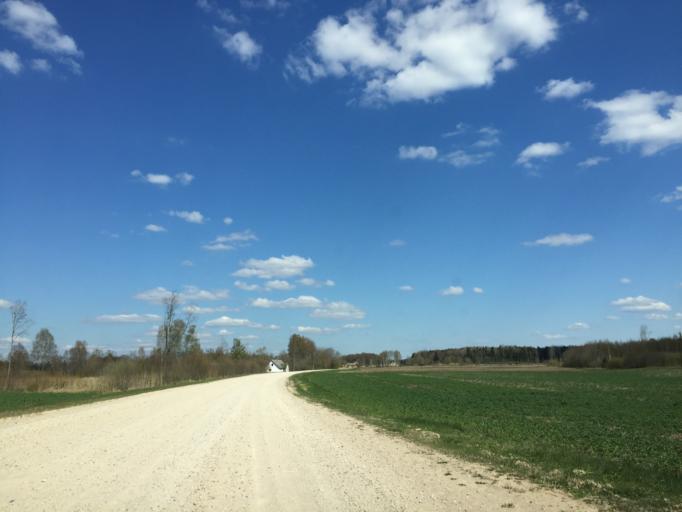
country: LV
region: Saulkrastu
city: Saulkrasti
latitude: 57.2504
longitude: 24.5204
